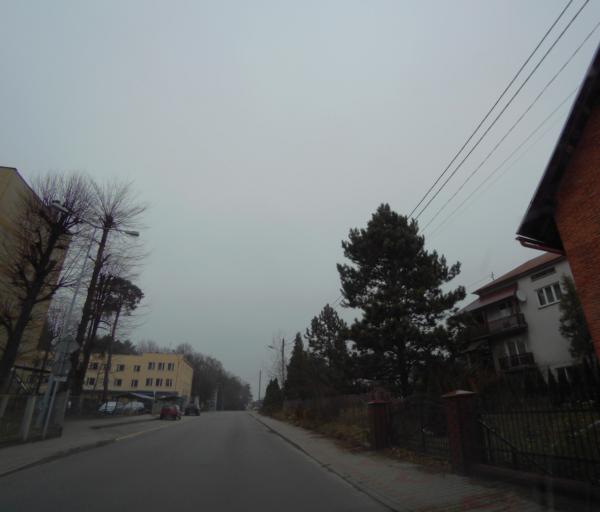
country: PL
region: Subcarpathian Voivodeship
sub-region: Powiat lezajski
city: Lezajsk
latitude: 50.2690
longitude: 22.4204
